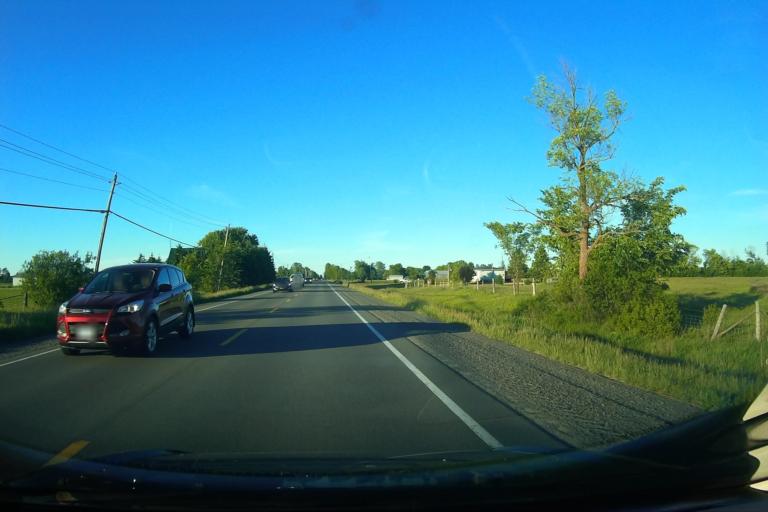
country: CA
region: Ontario
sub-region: Lanark County
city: Smiths Falls
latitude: 44.9751
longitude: -75.7409
